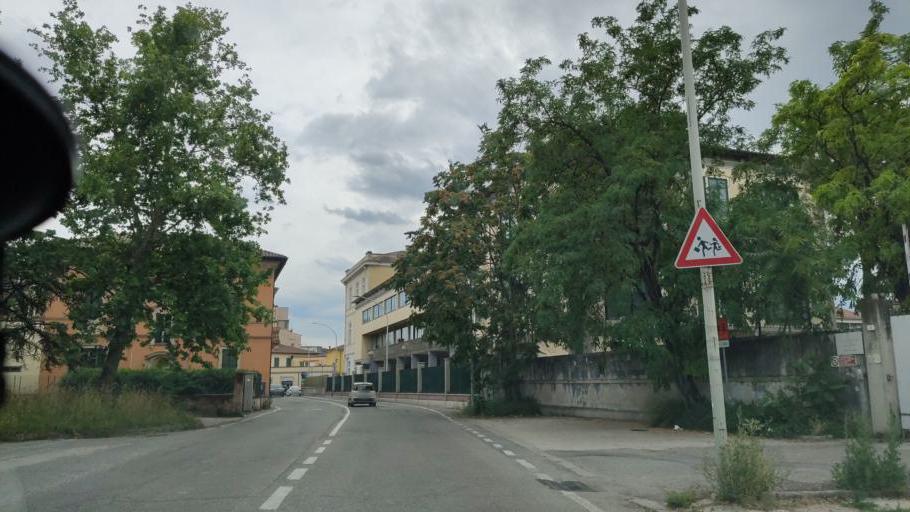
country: IT
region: Umbria
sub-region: Provincia di Terni
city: Terni
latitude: 42.5661
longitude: 12.6564
